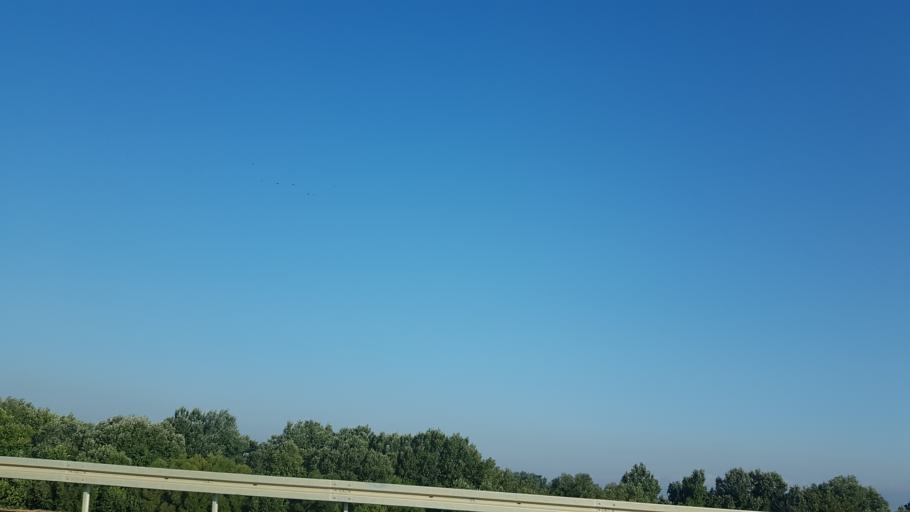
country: TR
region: Bursa
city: Karacabey
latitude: 40.1821
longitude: 28.3310
